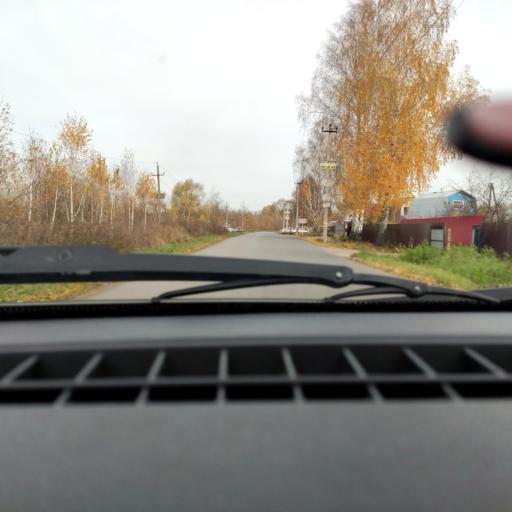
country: RU
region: Bashkortostan
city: Iglino
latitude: 54.8107
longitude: 56.1891
